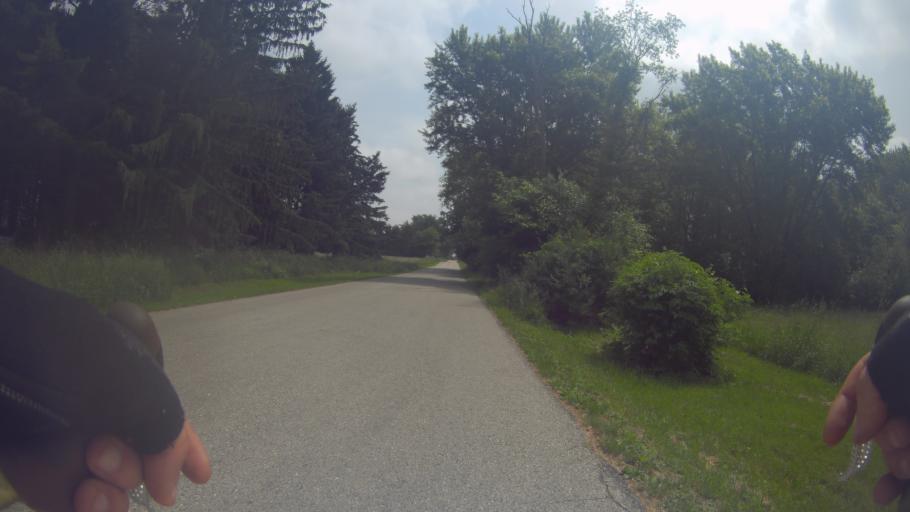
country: US
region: Wisconsin
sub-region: Jefferson County
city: Cambridge
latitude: 42.9314
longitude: -88.9976
